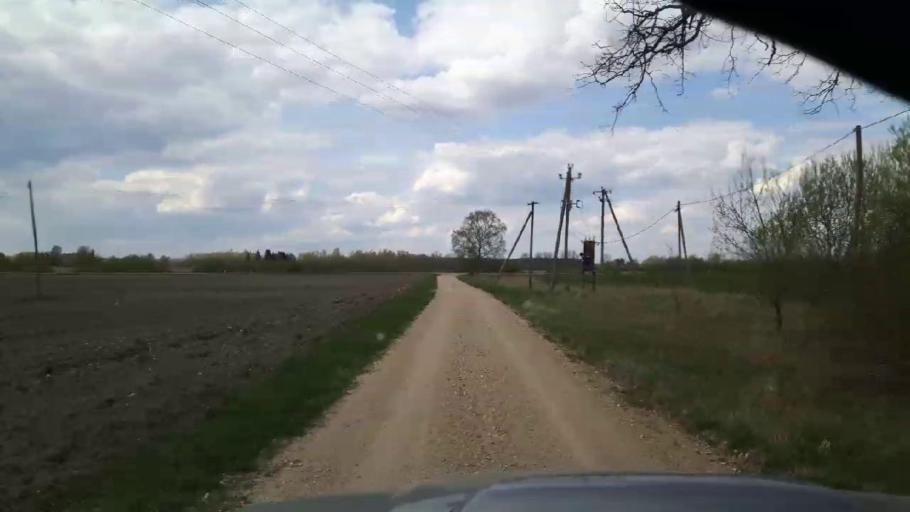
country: EE
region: Paernumaa
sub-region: Sindi linn
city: Sindi
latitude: 58.4162
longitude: 24.7000
